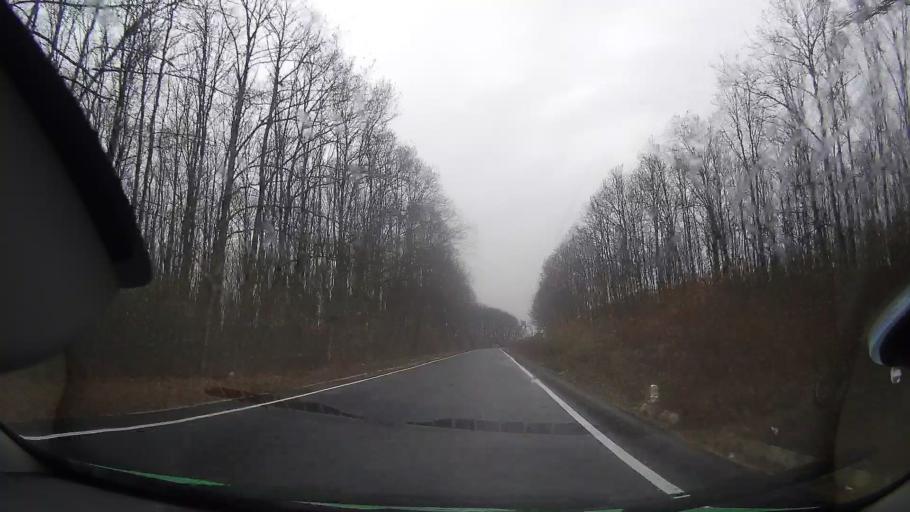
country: RO
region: Bihor
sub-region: Comuna Olcea
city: Olcea
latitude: 46.7001
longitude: 21.9645
